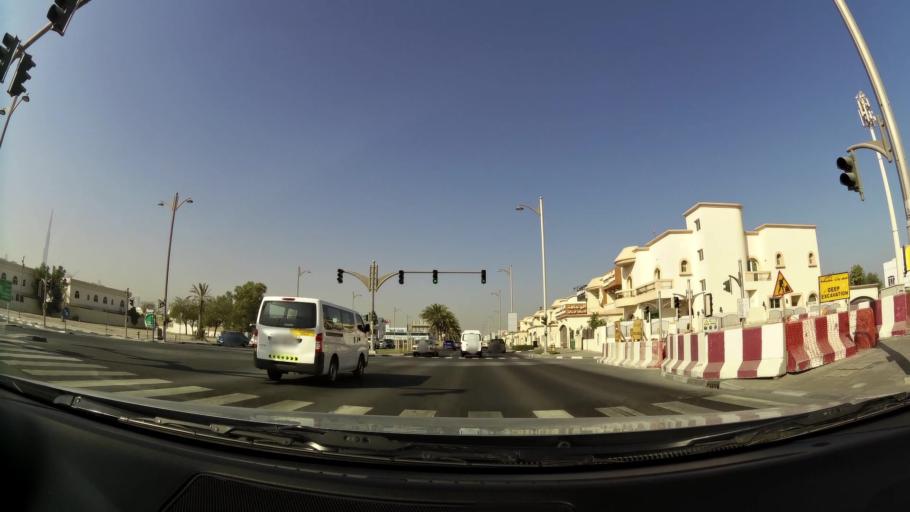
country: AE
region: Dubai
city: Dubai
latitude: 25.2277
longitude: 55.2601
